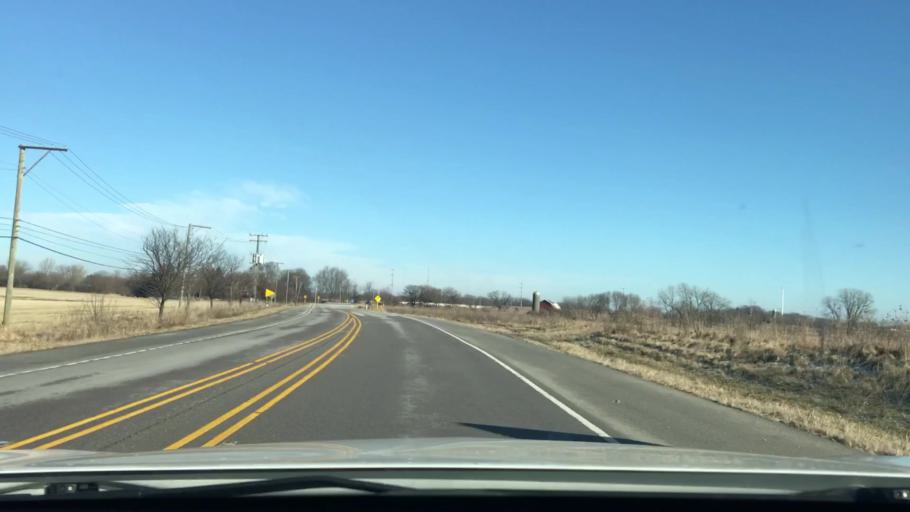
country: US
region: Illinois
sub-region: Kane County
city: Gilberts
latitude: 42.0975
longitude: -88.3987
